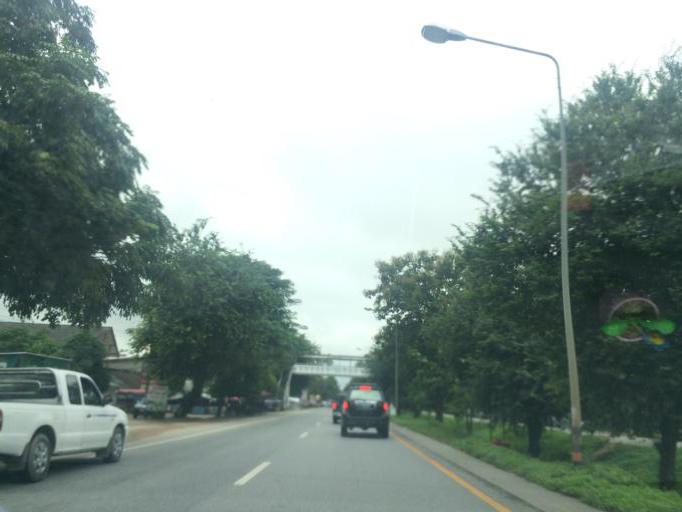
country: TH
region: Chiang Rai
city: Mae Lao
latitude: 19.7738
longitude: 99.7389
